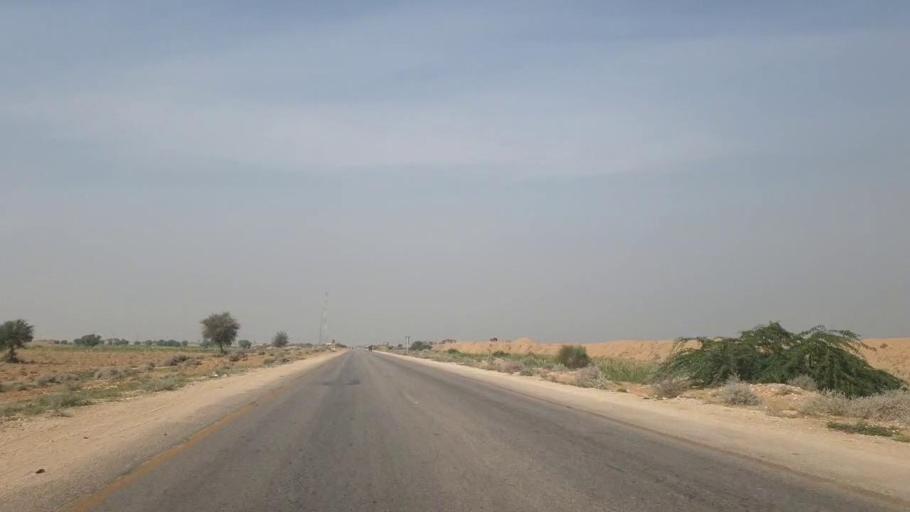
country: PK
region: Sindh
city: Sann
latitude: 26.0449
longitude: 68.1109
